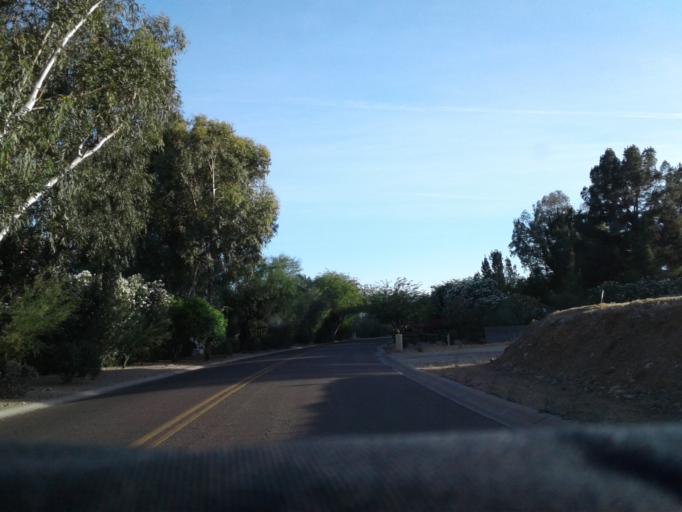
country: US
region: Arizona
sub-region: Maricopa County
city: Paradise Valley
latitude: 33.5301
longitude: -111.9965
